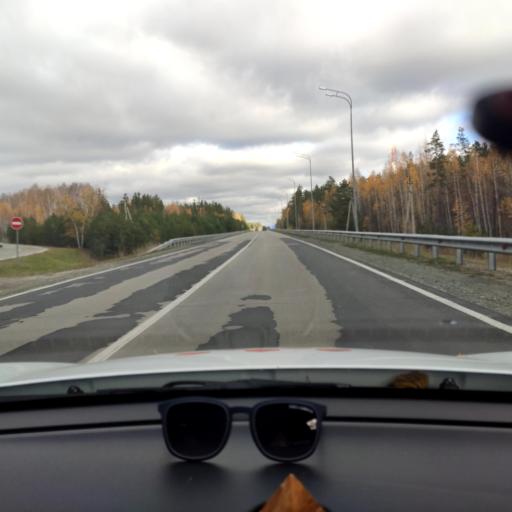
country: RU
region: Tatarstan
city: Stolbishchi
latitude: 55.6353
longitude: 49.1057
